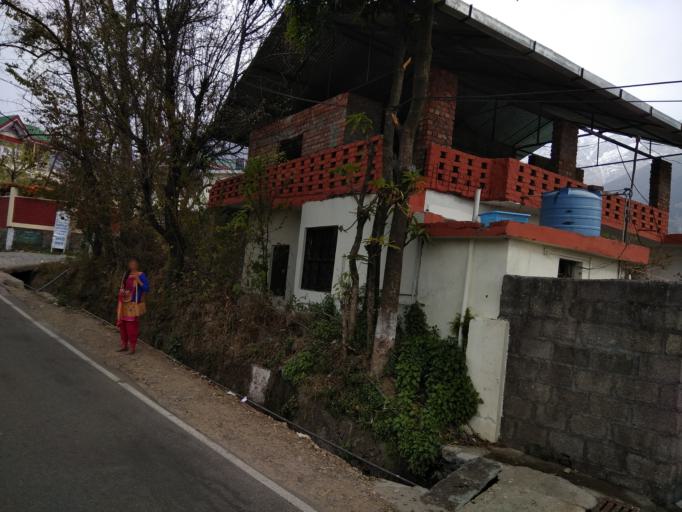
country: IN
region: Himachal Pradesh
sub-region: Kangra
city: Dharmsala
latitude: 32.2011
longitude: 76.3344
